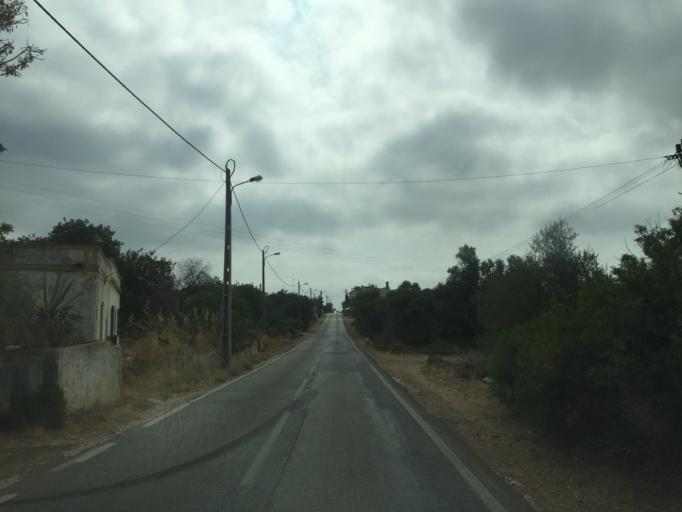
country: PT
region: Faro
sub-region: Faro
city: Santa Barbara de Nexe
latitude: 37.0975
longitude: -7.9548
